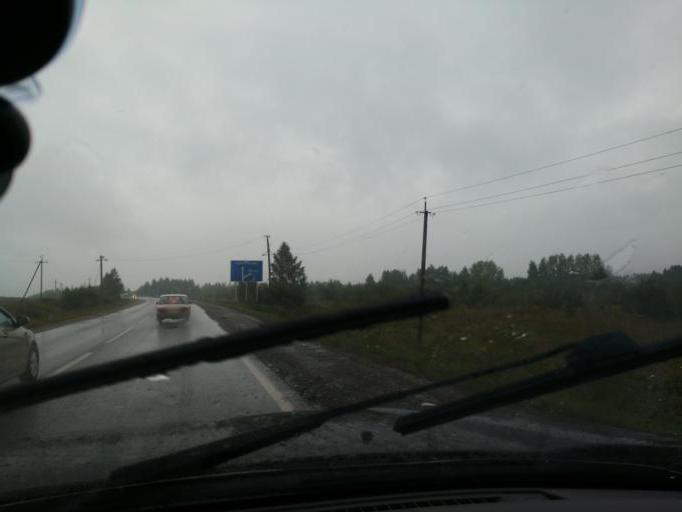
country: RU
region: Perm
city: Osa
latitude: 57.1746
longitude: 55.5323
